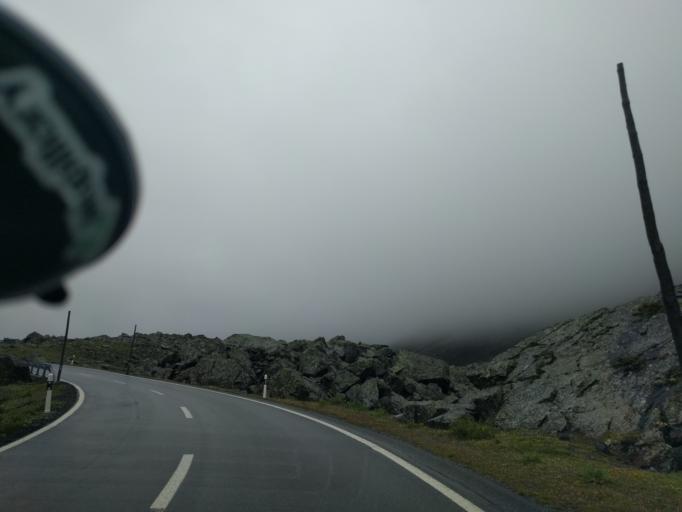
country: CH
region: Grisons
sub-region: Praettigau/Davos District
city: Davos
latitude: 46.7542
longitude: 9.9413
